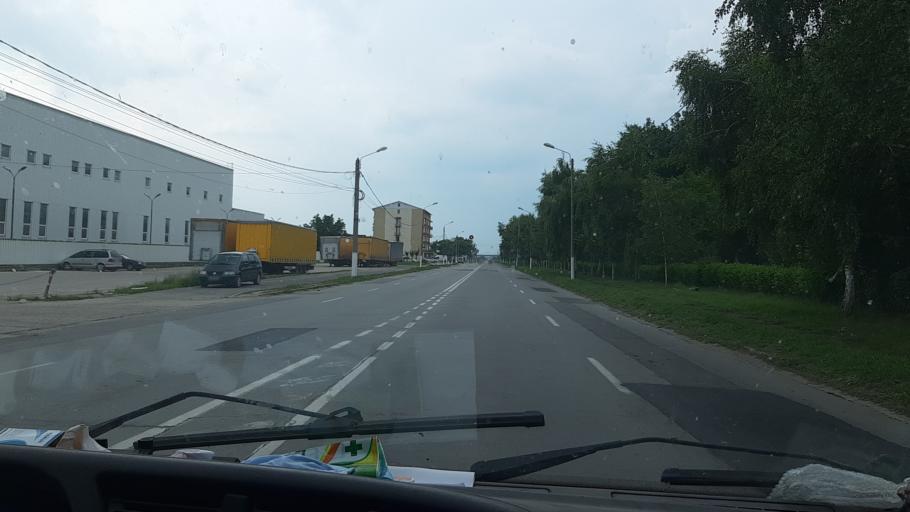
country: RO
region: Timis
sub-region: Municipiul Lugoj
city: Lugoj
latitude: 45.7073
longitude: 21.8881
